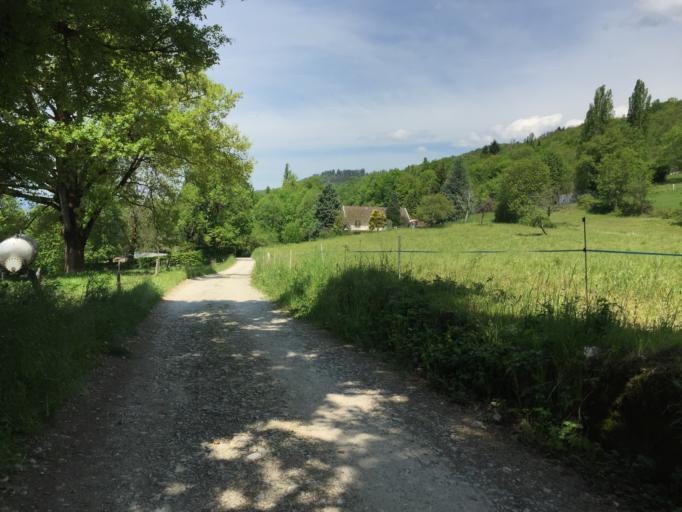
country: FR
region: Rhone-Alpes
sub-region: Departement de la Savoie
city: Mouxy
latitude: 45.6688
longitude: 5.9441
